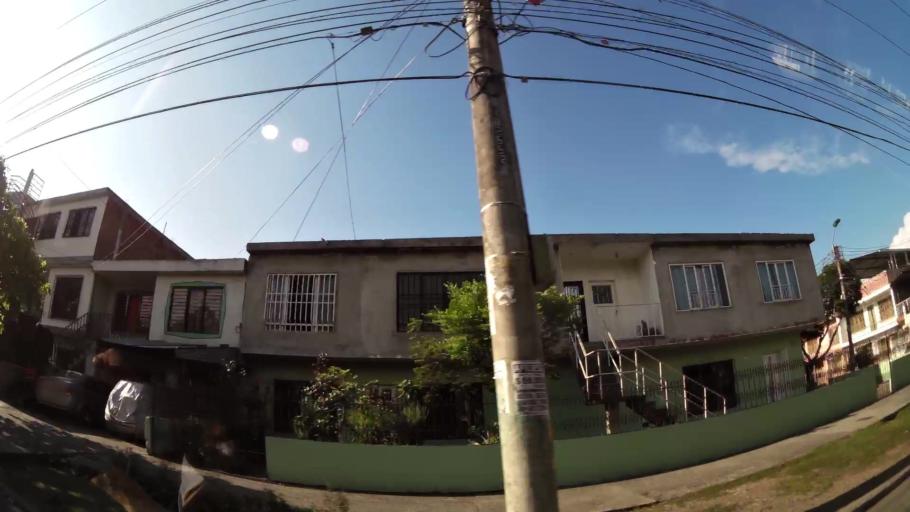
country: CO
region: Valle del Cauca
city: Cali
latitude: 3.4282
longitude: -76.5125
